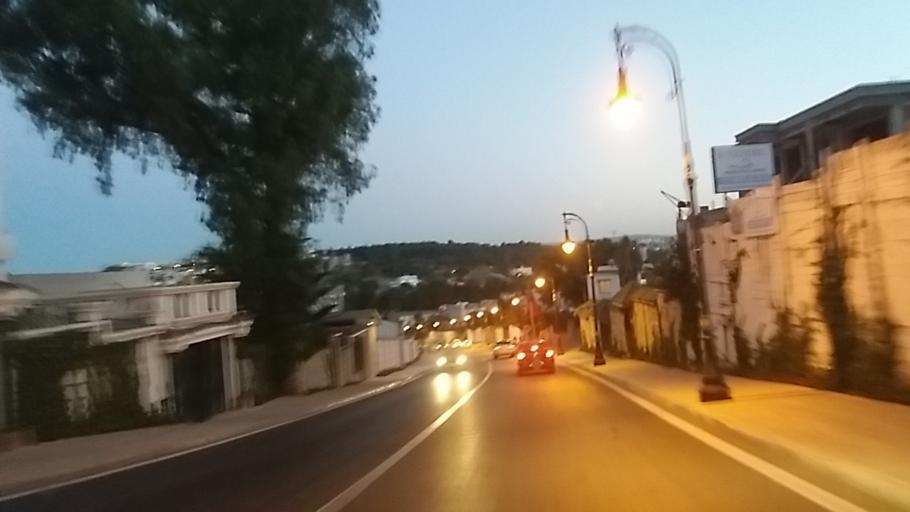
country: MA
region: Tanger-Tetouan
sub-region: Tanger-Assilah
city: Tangier
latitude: 35.7841
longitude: -5.8432
